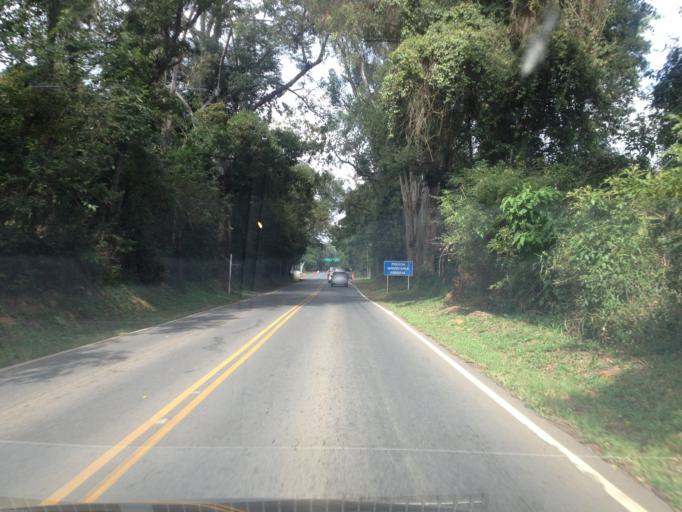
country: BR
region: Minas Gerais
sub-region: Itanhandu
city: Itanhandu
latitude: -22.2433
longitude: -44.9353
